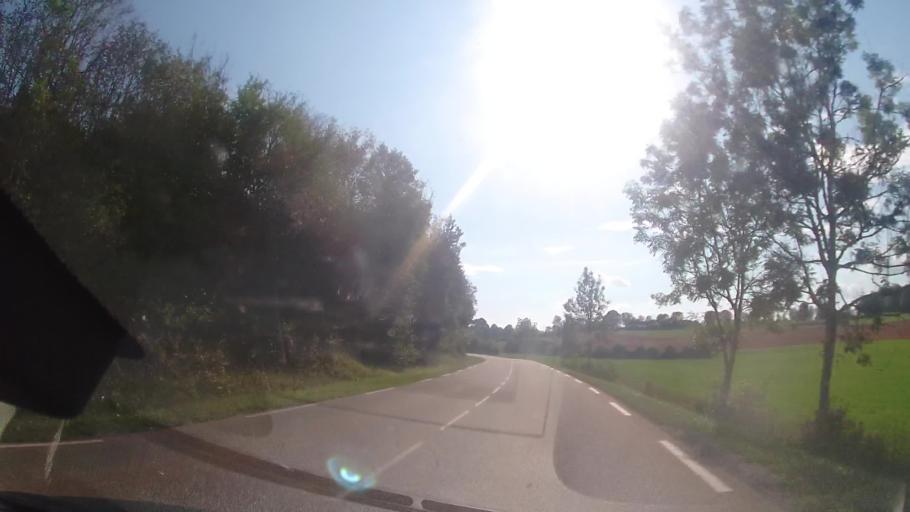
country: FR
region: Franche-Comte
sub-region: Departement du Jura
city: Clairvaux-les-Lacs
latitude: 46.5908
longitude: 5.8378
